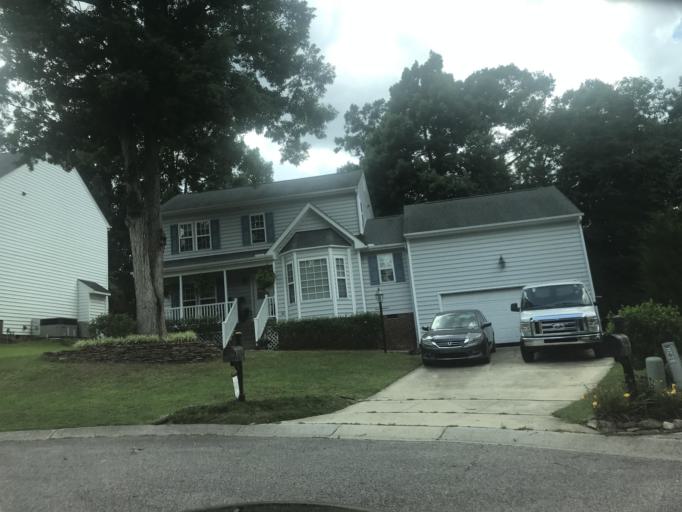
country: US
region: North Carolina
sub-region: Wake County
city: Knightdale
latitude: 35.8375
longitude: -78.5646
